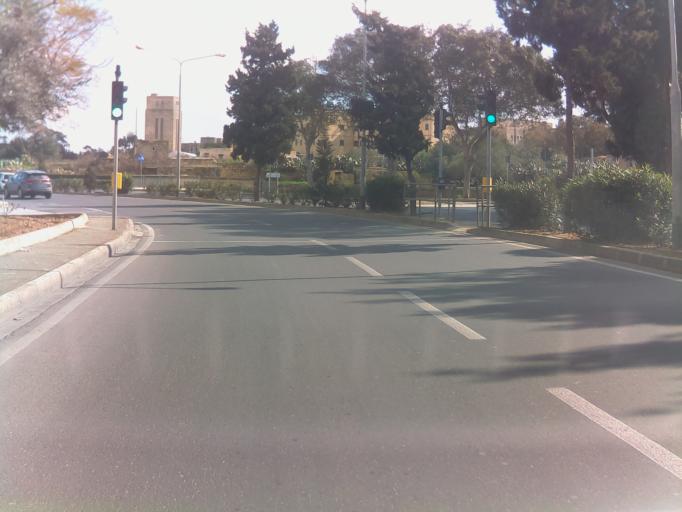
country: MT
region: Luqa
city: Luqa
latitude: 35.8559
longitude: 14.4869
